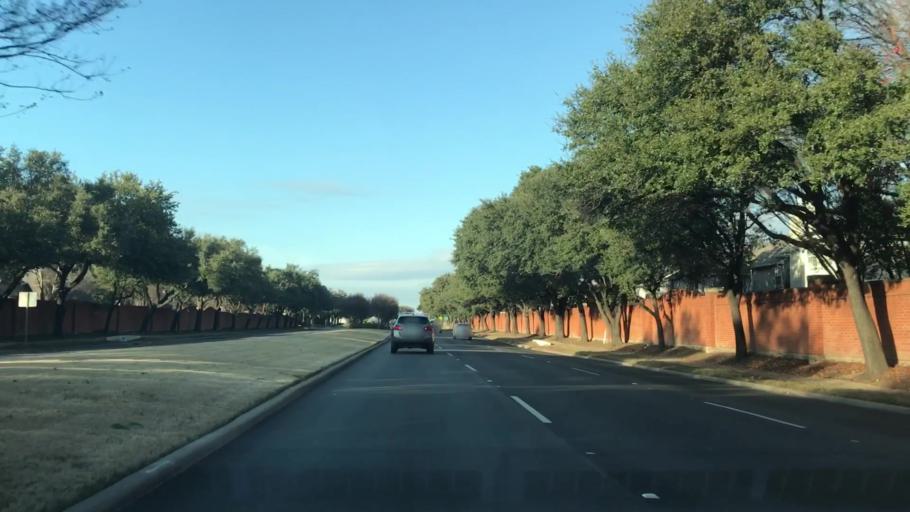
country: US
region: Texas
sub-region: Dallas County
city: Farmers Branch
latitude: 32.9368
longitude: -96.9520
